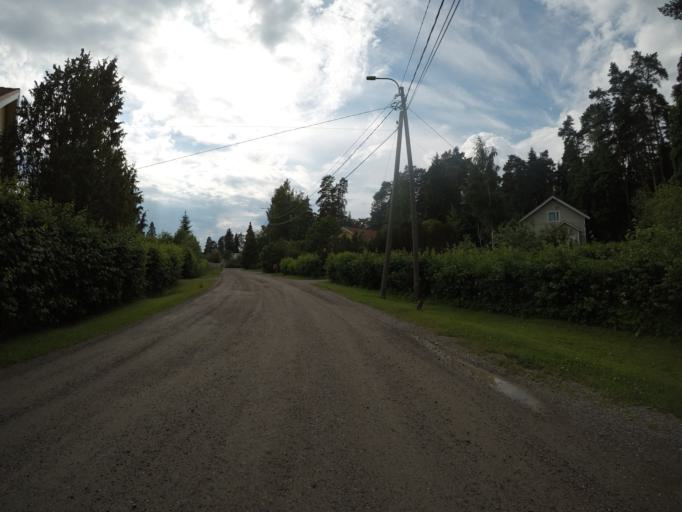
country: FI
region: Haeme
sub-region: Haemeenlinna
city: Haemeenlinna
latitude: 61.0126
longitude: 24.4821
